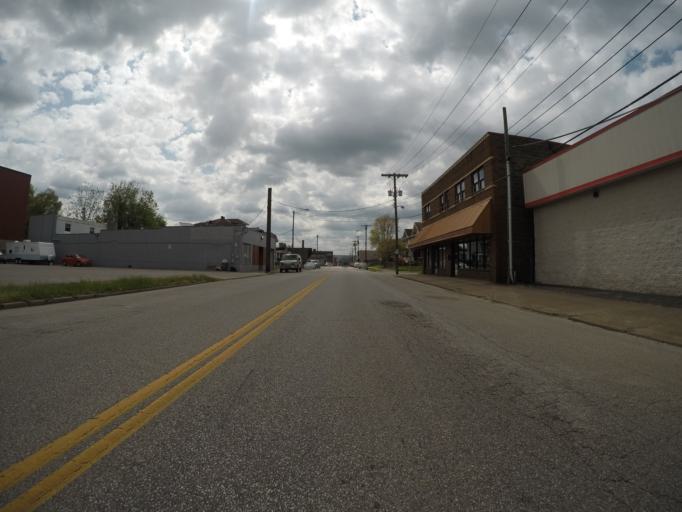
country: US
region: West Virginia
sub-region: Kanawha County
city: Charleston
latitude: 38.3646
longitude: -81.6510
